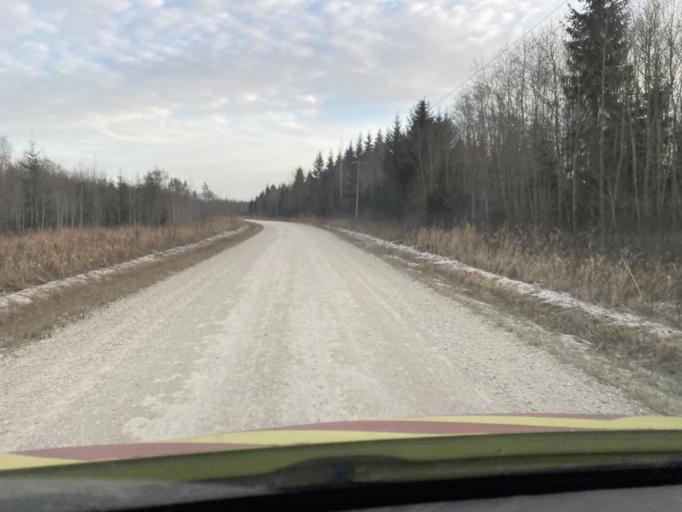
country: EE
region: Jogevamaa
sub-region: Poltsamaa linn
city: Poltsamaa
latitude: 58.5859
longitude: 26.0428
